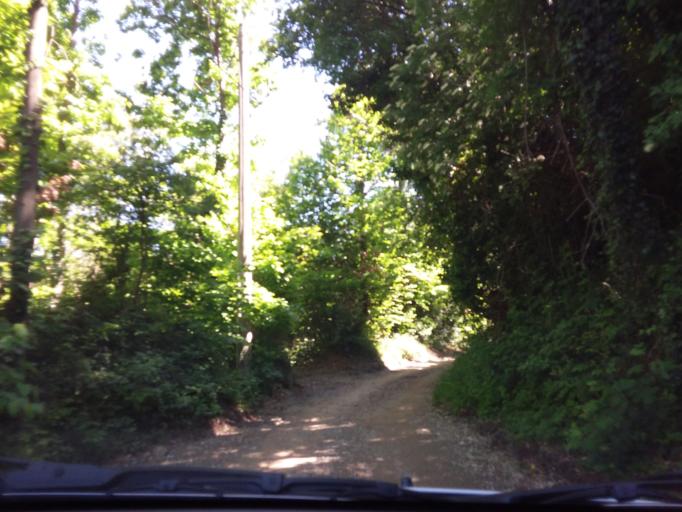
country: IT
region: Piedmont
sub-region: Provincia di Torino
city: Rosta
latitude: 45.0611
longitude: 7.4912
